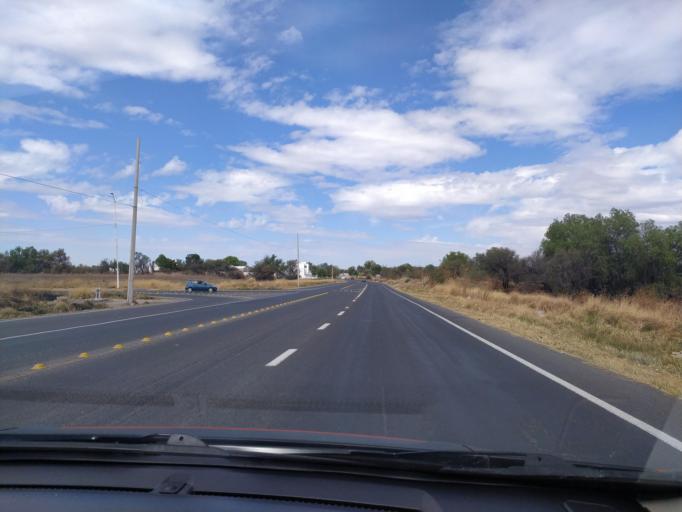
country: LA
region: Oudomxai
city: Muang La
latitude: 21.0109
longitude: 101.8288
